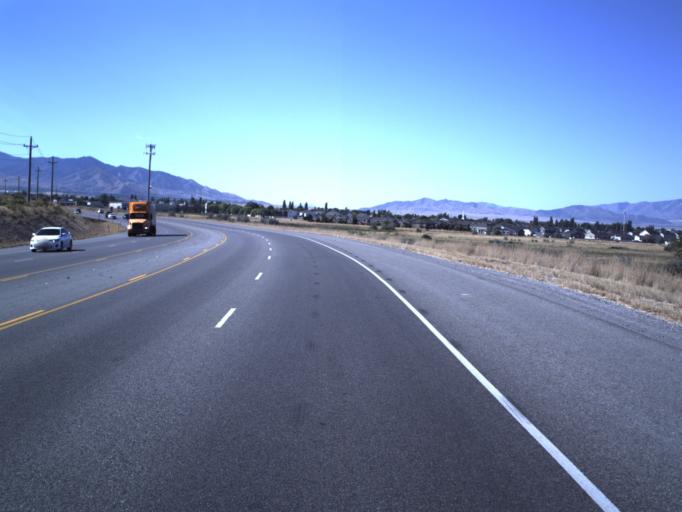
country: US
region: Utah
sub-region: Tooele County
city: Stansbury park
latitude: 40.6605
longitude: -112.2894
